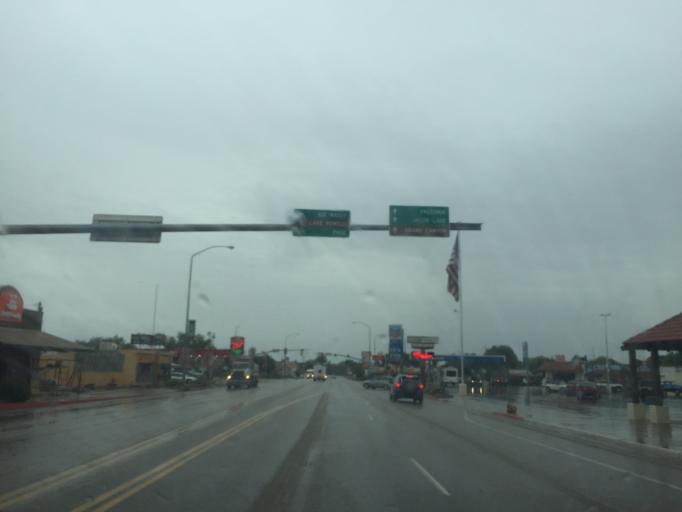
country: US
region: Utah
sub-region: Kane County
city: Kanab
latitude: 37.0443
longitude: -112.5264
